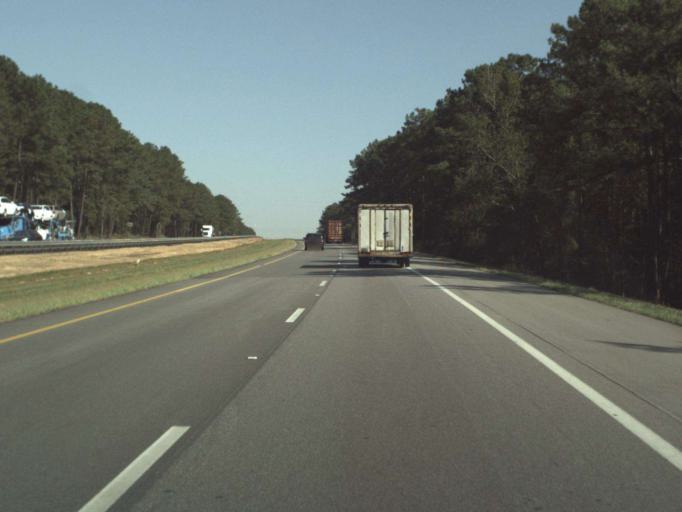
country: US
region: Florida
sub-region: Walton County
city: DeFuniak Springs
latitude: 30.6936
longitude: -86.1423
